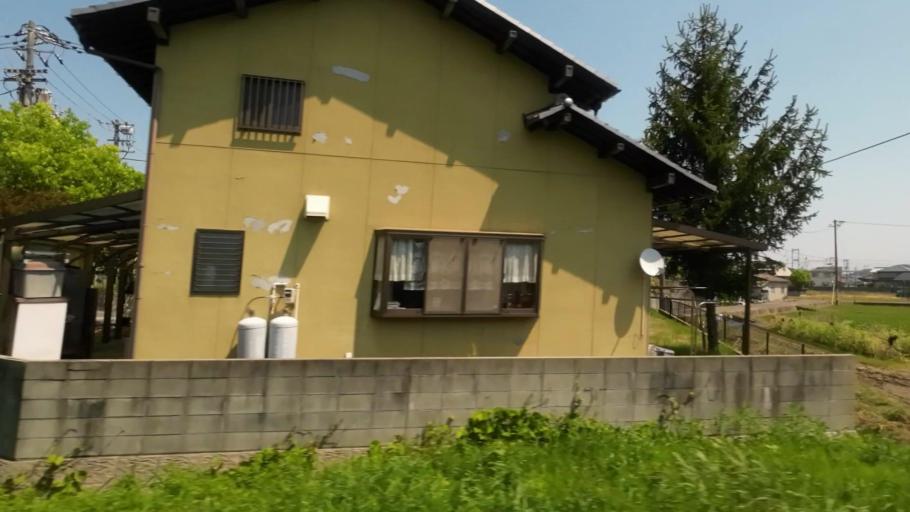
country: JP
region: Ehime
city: Hojo
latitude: 34.0969
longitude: 132.9519
